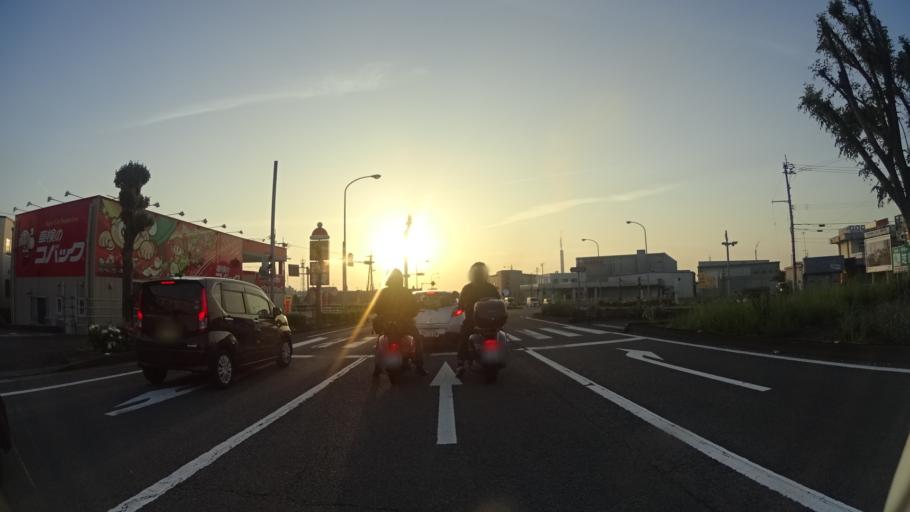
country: JP
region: Ehime
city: Kawanoecho
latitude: 33.9863
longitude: 133.5690
